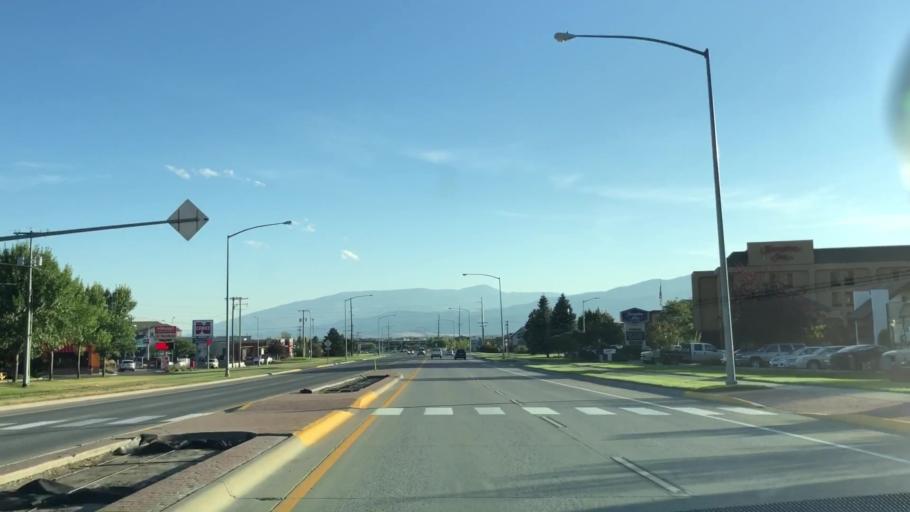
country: US
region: Montana
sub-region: Missoula County
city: Orchard Homes
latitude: 46.9093
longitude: -114.0363
